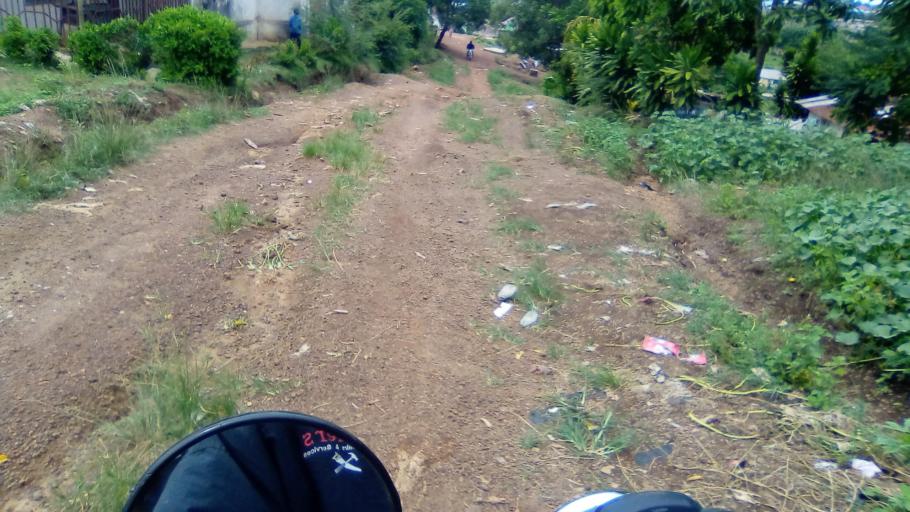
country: SL
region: Southern Province
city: Bo
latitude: 7.9361
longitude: -11.7195
